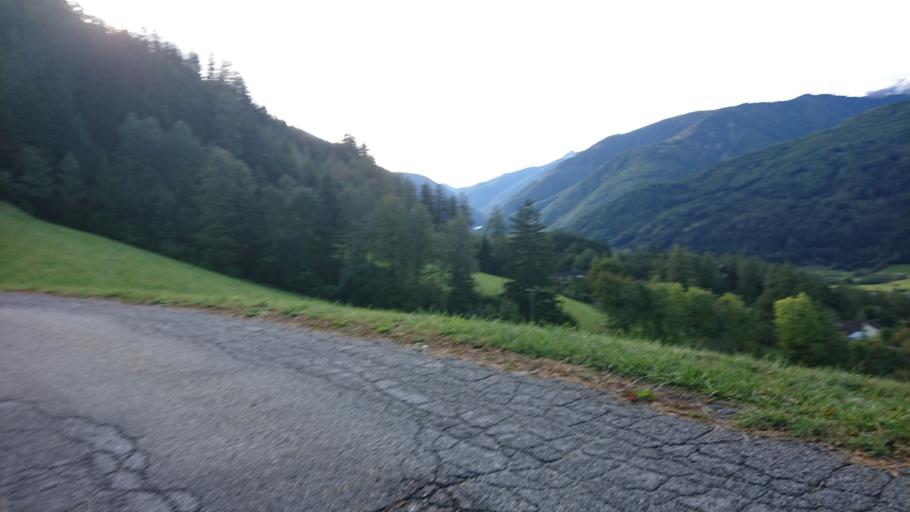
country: IT
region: Trentino-Alto Adige
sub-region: Bolzano
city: Campo di Trens
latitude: 46.8791
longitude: 11.4874
